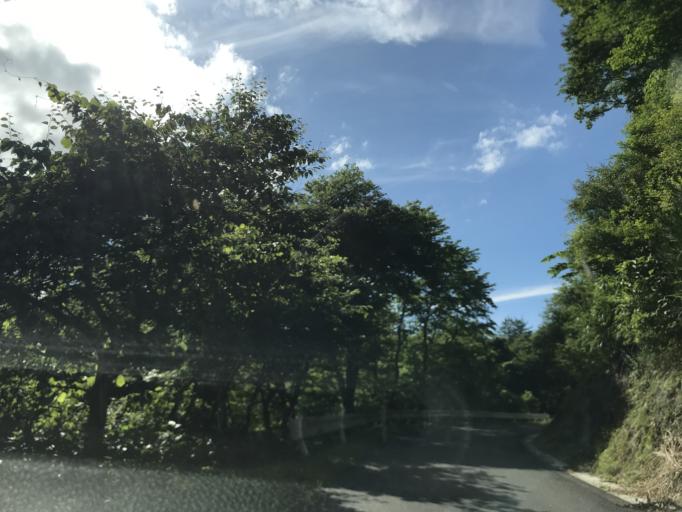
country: JP
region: Iwate
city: Ichinoseki
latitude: 38.9216
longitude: 140.9599
